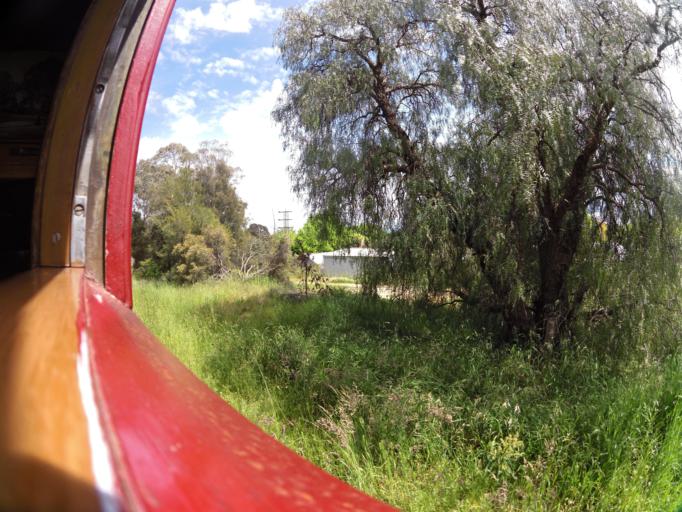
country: AU
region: Victoria
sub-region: Mount Alexander
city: Castlemaine
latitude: -37.0730
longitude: 144.2086
